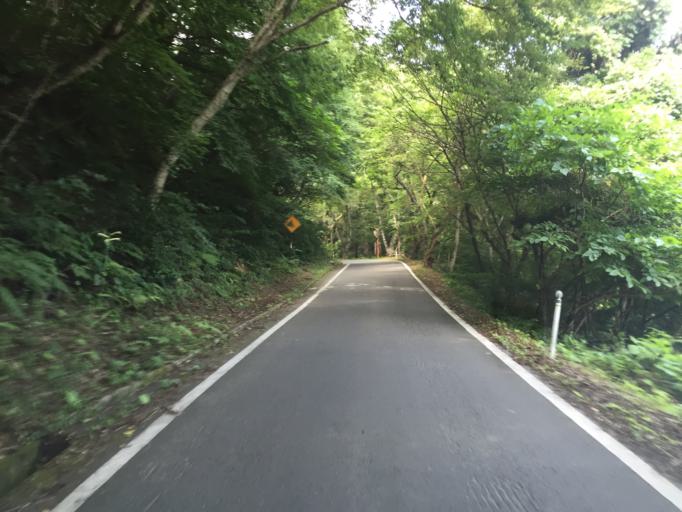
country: JP
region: Fukushima
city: Inawashiro
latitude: 37.4135
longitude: 140.1087
